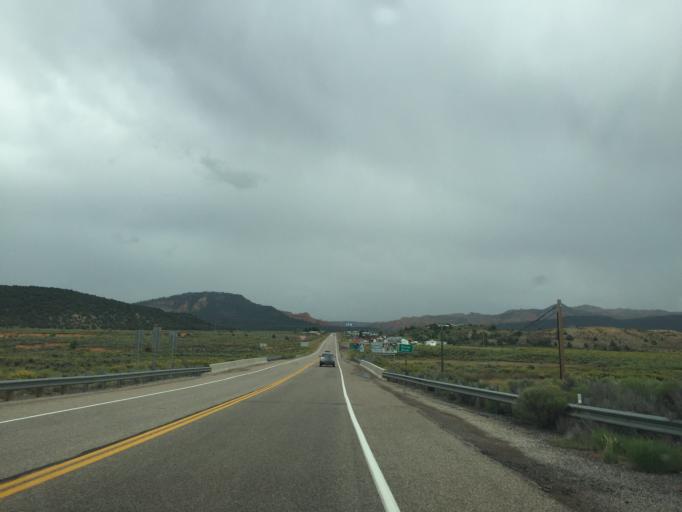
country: US
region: Utah
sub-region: Garfield County
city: Panguitch
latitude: 37.7496
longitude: -112.3758
